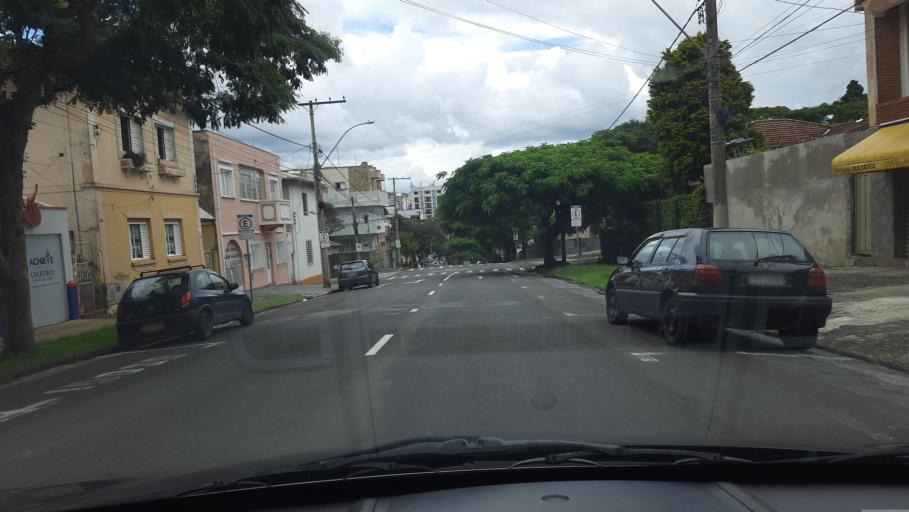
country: BR
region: Minas Gerais
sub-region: Pocos De Caldas
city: Pocos de Caldas
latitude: -21.7816
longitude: -46.5680
